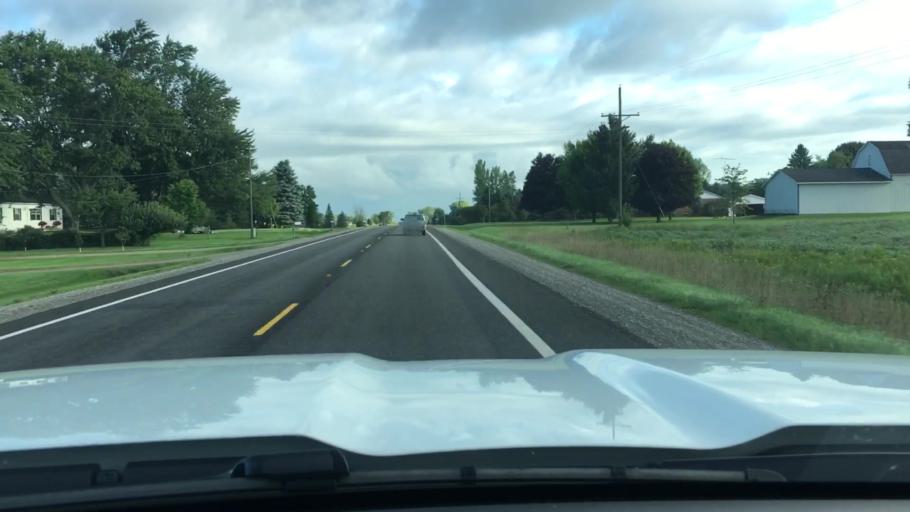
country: US
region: Michigan
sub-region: Tuscola County
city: Caro
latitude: 43.3987
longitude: -83.3836
